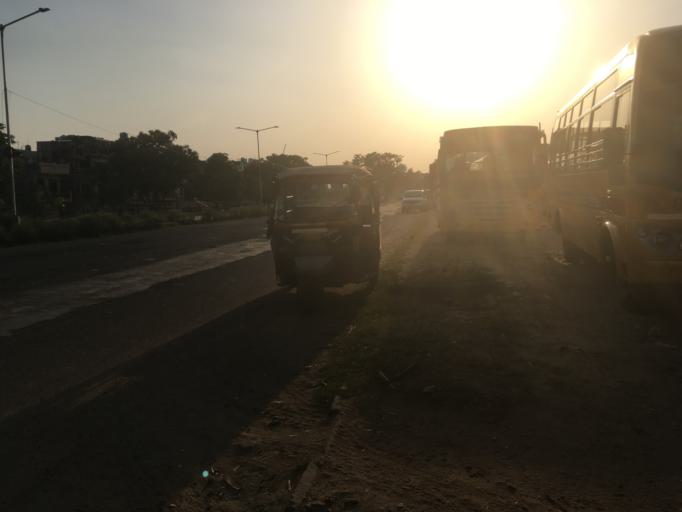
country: IN
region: Chandigarh
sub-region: Chandigarh
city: Chandigarh
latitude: 30.7015
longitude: 76.8319
